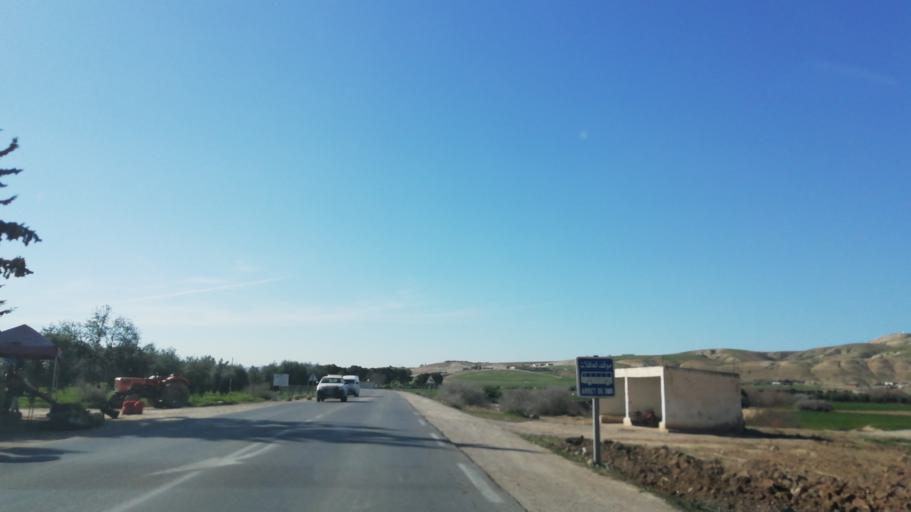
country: DZ
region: Mascara
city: Oued el Abtal
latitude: 35.4581
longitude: 0.7533
